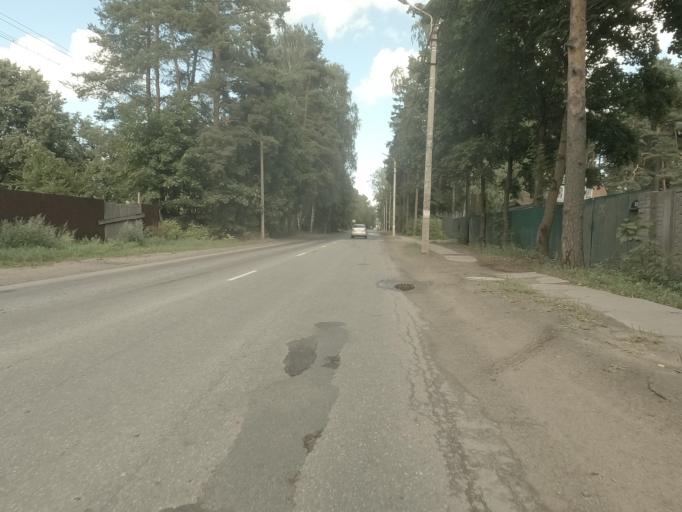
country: RU
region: Leningrad
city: Vsevolozhsk
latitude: 60.0157
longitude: 30.6722
